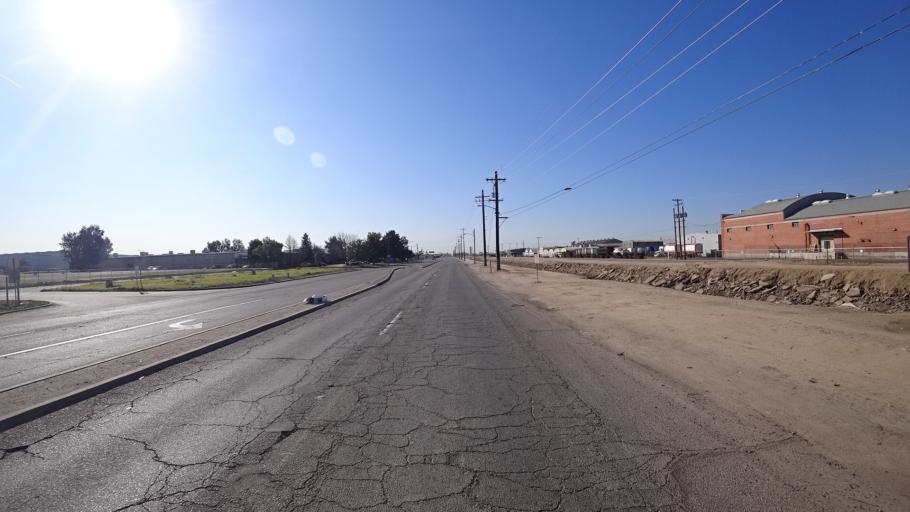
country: US
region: California
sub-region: Fresno County
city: Fresno
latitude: 36.7065
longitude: -119.7365
